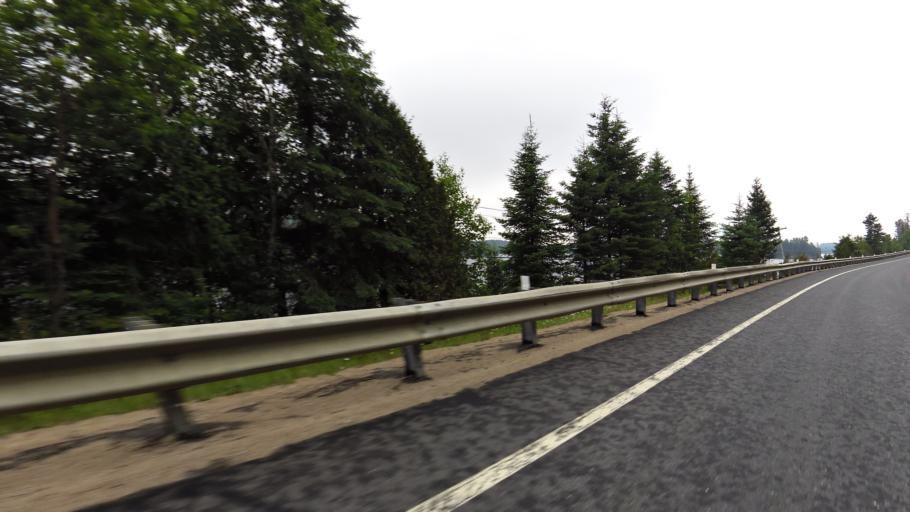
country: CA
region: Ontario
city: Huntsville
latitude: 45.5009
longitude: -78.7413
